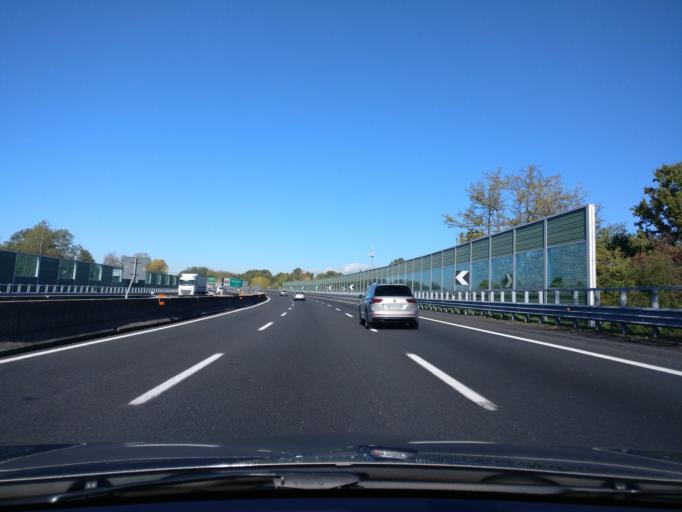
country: IT
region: Latium
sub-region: Provincia di Frosinone
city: Frosinone
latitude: 41.6121
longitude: 13.3292
